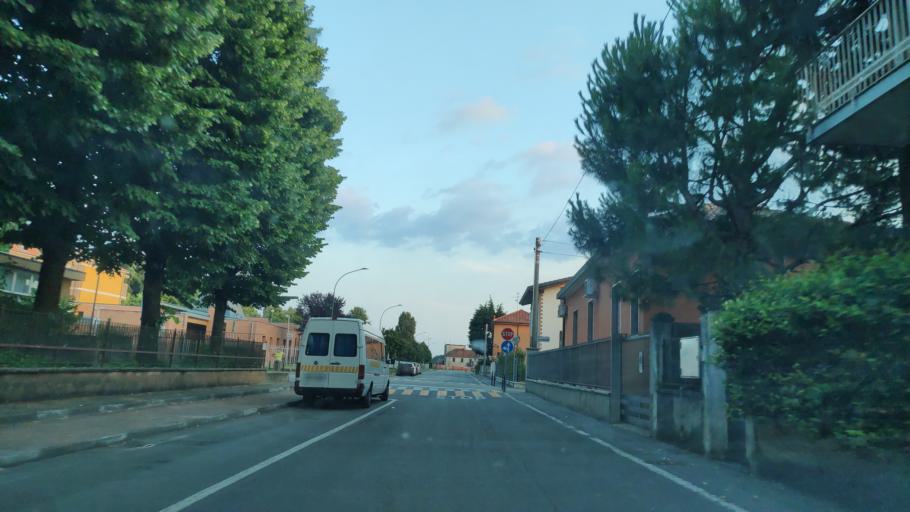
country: IT
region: Lombardy
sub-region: Citta metropolitana di Milano
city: Melzo
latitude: 45.4953
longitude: 9.4258
